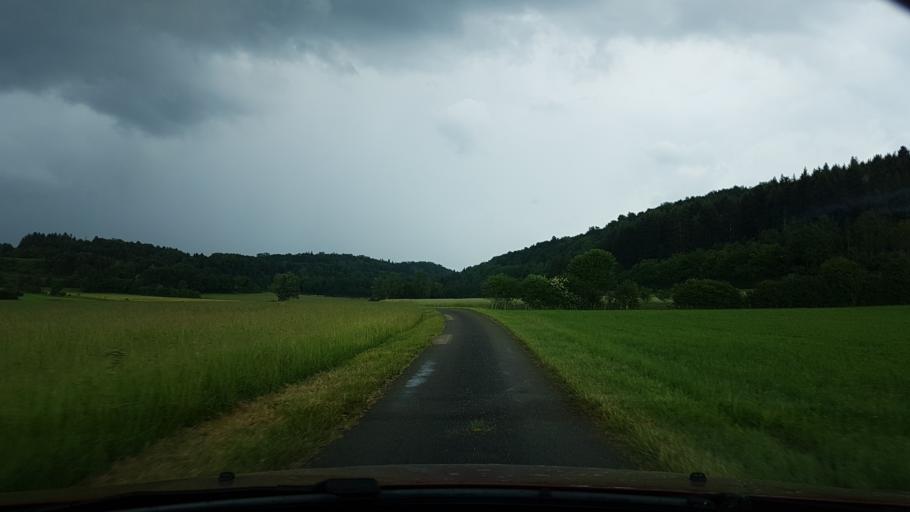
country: FR
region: Franche-Comte
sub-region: Departement du Jura
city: Clairvaux-les-Lacs
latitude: 46.5421
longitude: 5.7025
